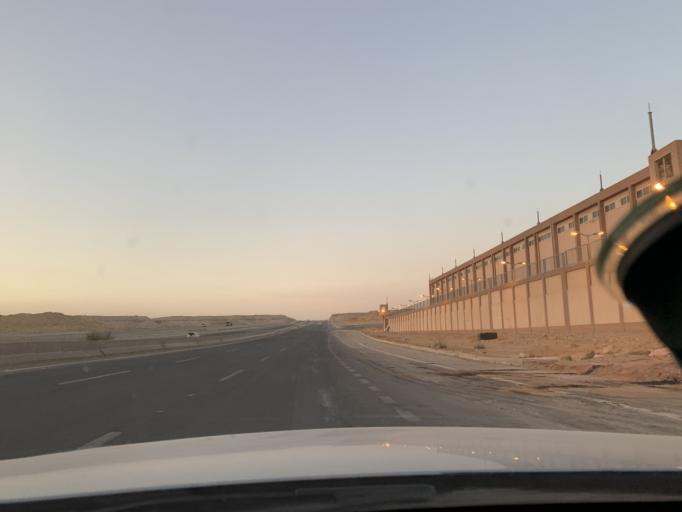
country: EG
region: Muhafazat al Qahirah
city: Halwan
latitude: 29.9380
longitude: 31.5297
